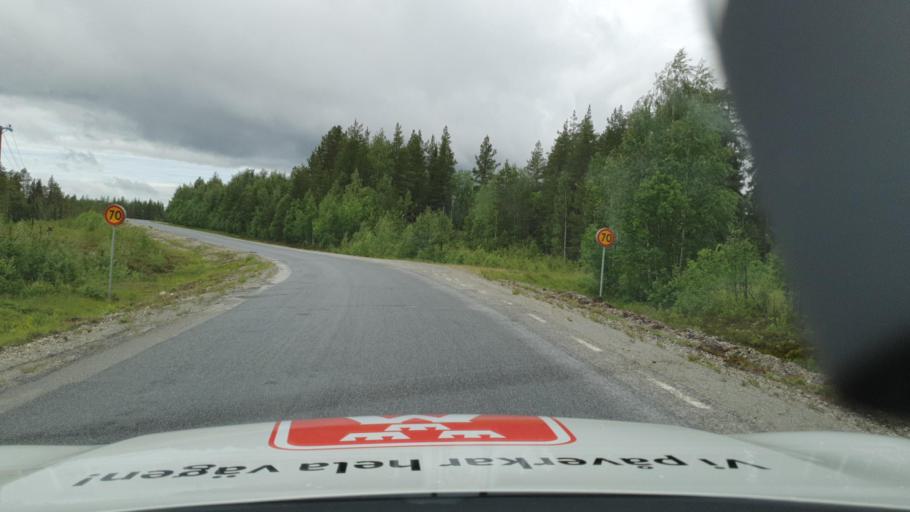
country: SE
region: Vaesterbotten
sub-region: Dorotea Kommun
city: Dorotea
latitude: 64.1860
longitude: 16.6224
